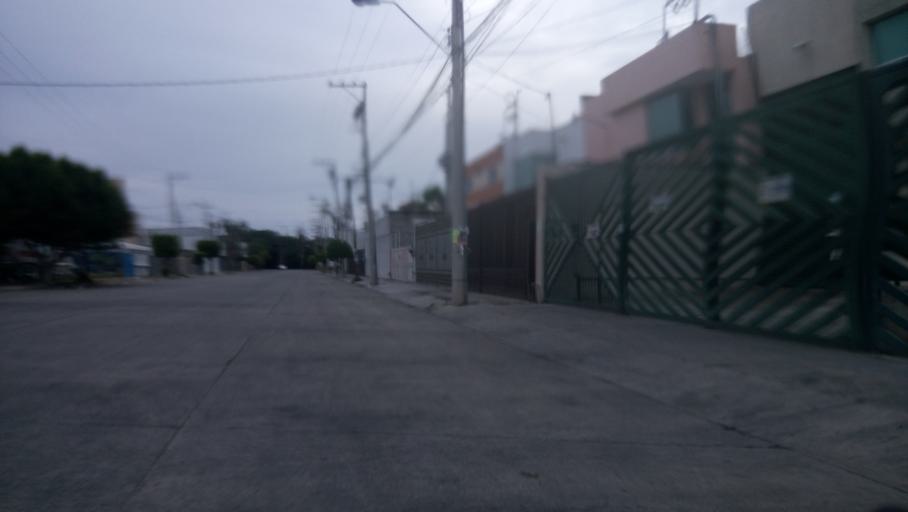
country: MX
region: Guanajuato
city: Leon
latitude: 21.1438
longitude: -101.6623
